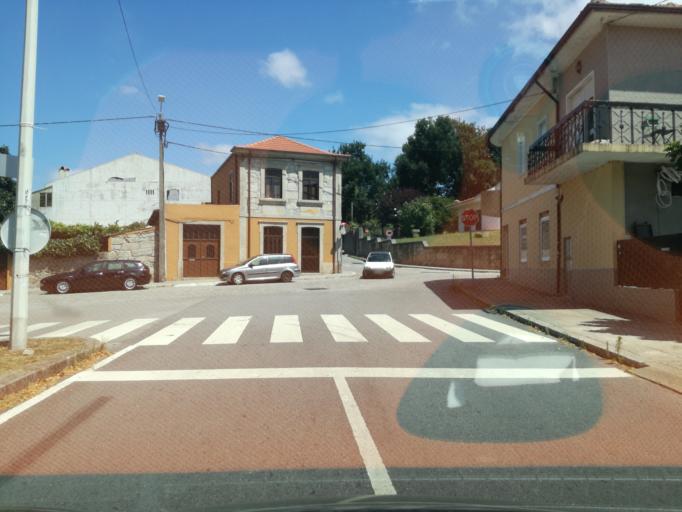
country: PT
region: Porto
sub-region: Maia
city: Maia
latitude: 41.2424
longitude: -8.6085
